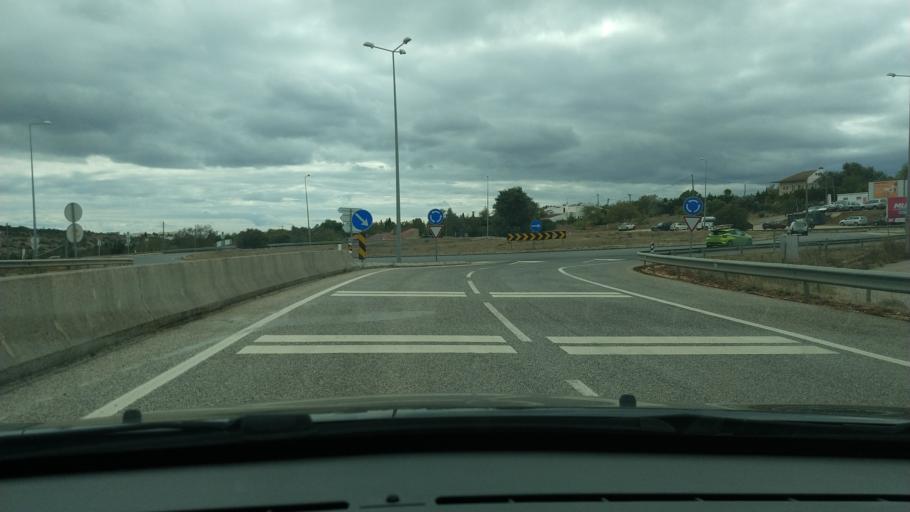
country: PT
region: Faro
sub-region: Lagos
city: Lagos
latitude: 37.1026
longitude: -8.6946
